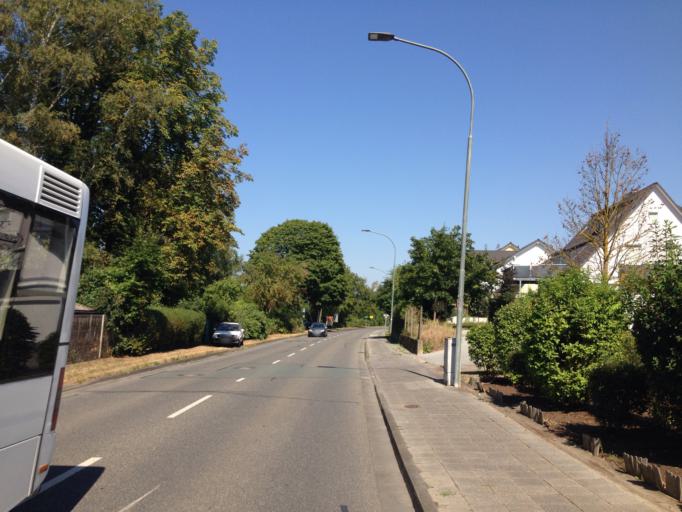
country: DE
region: Hesse
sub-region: Regierungsbezirk Giessen
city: Giessen
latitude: 50.6020
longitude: 8.6726
